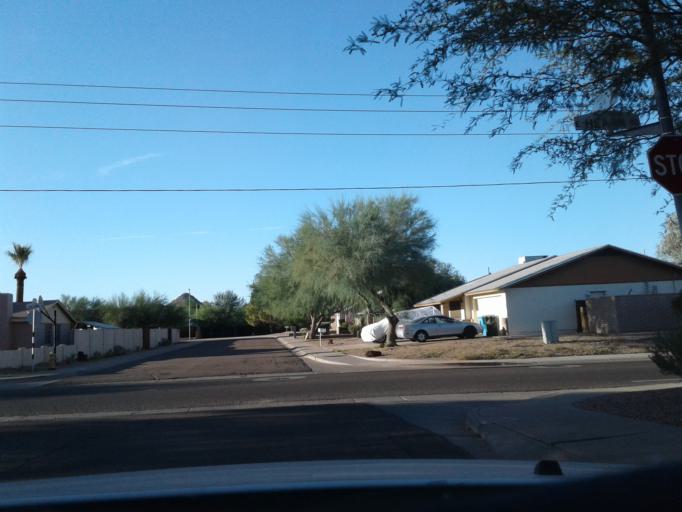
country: US
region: Arizona
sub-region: Maricopa County
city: Paradise Valley
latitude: 33.6149
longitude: -112.0616
